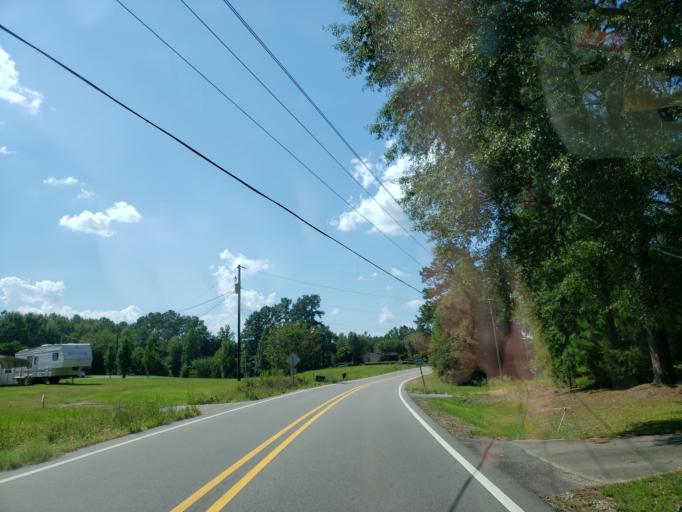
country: US
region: Mississippi
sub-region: Lamar County
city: Sumrall
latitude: 31.4025
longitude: -89.5429
